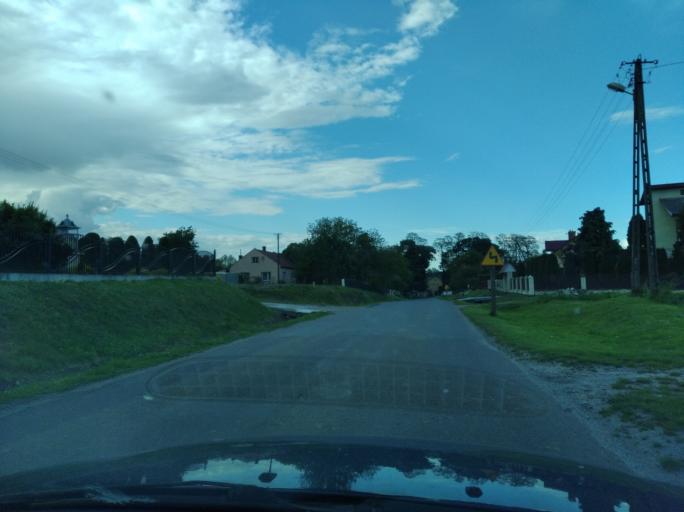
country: PL
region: Subcarpathian Voivodeship
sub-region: Powiat jaroslawski
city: Rokietnica
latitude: 49.9373
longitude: 22.6664
